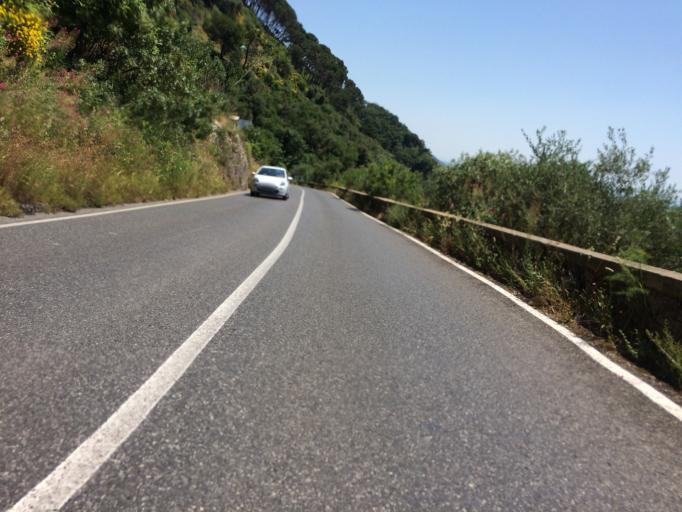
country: IT
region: Tuscany
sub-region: Provincia di Massa-Carrara
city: Massa
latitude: 44.0577
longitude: 10.1215
